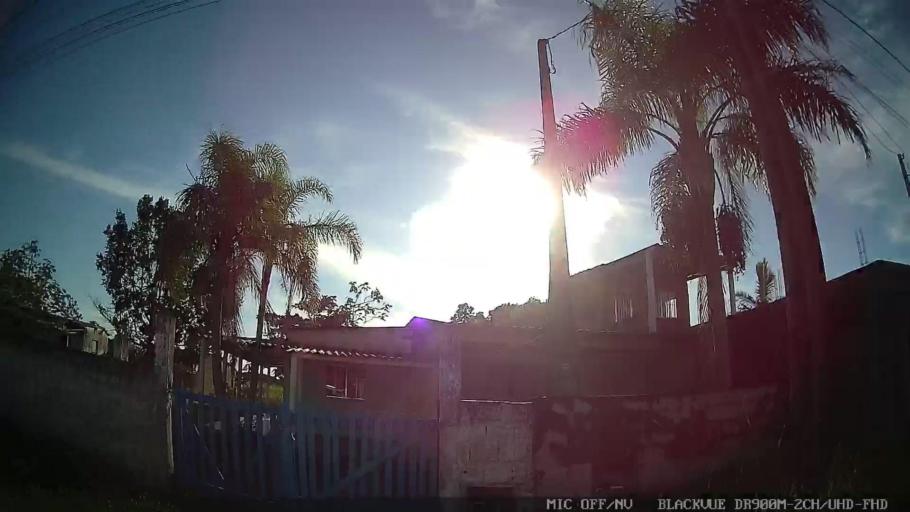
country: BR
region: Sao Paulo
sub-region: Iguape
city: Iguape
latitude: -24.7557
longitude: -47.5743
